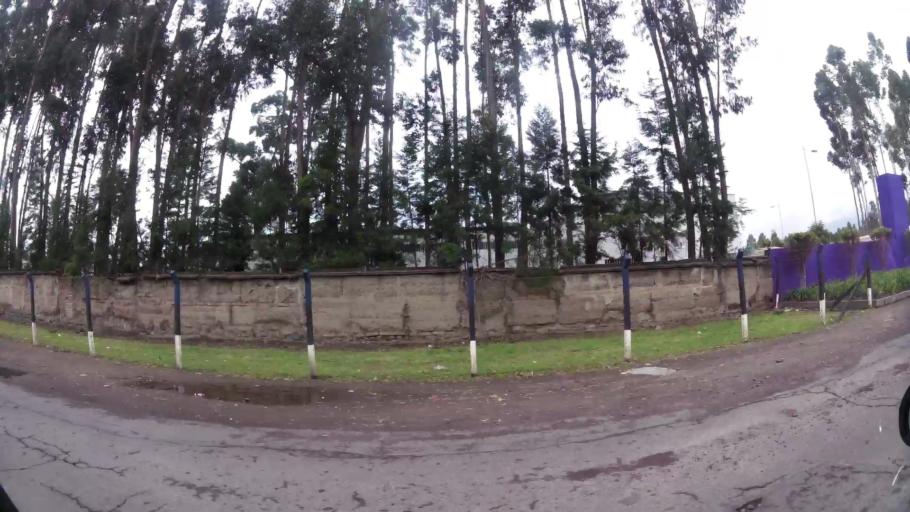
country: EC
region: Pichincha
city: Sangolqui
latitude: -0.3469
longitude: -78.4708
